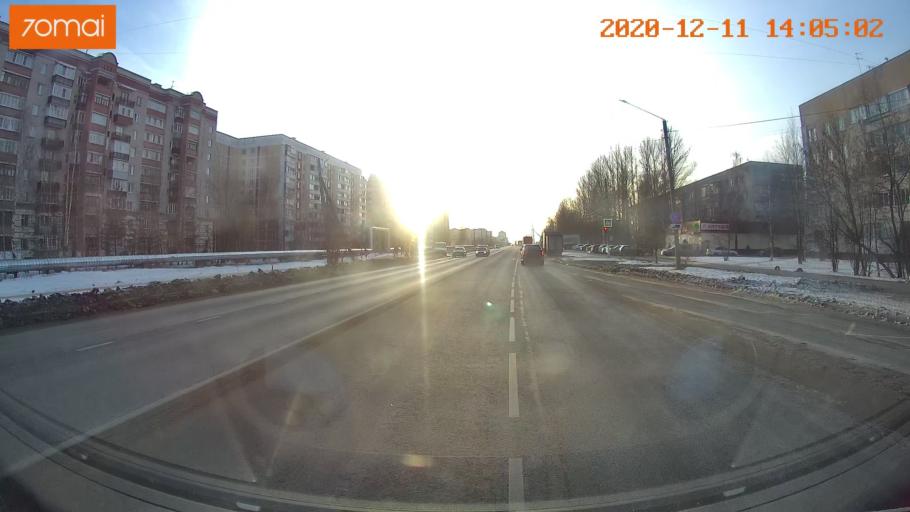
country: RU
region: Kostroma
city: Oktyabr'skiy
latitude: 57.7500
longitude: 41.0159
